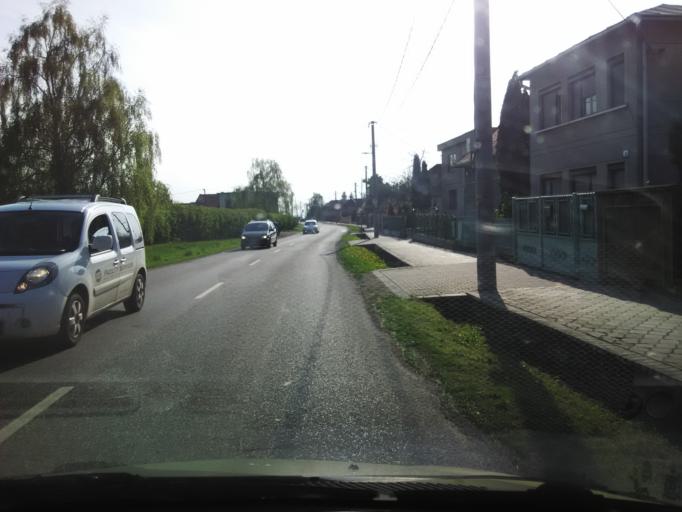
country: SK
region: Nitriansky
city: Levice
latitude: 48.2739
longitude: 18.6317
